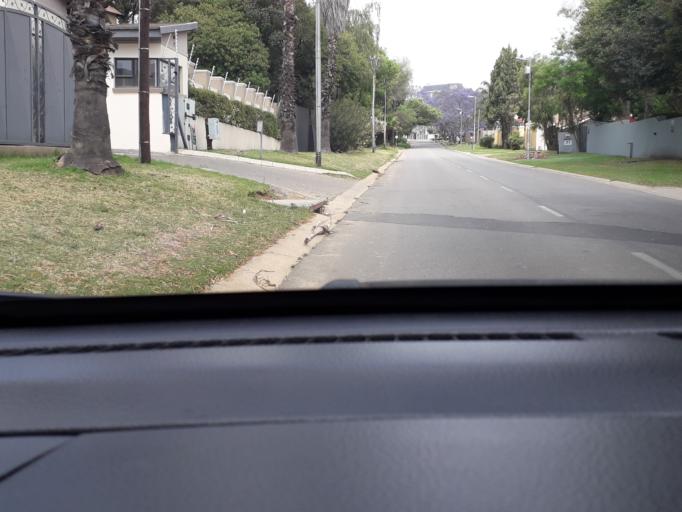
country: ZA
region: Gauteng
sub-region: City of Johannesburg Metropolitan Municipality
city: Modderfontein
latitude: -26.0928
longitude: 28.0625
